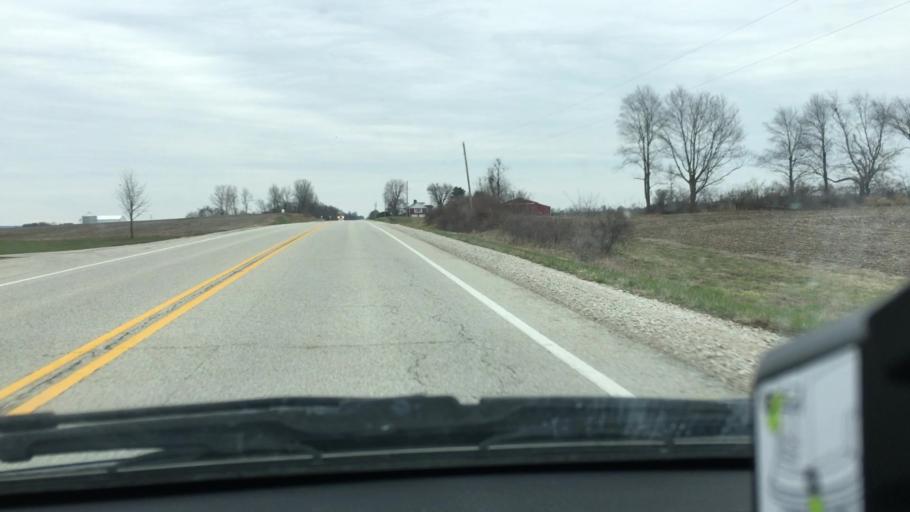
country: US
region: Indiana
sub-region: Daviess County
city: Odon
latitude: 38.9404
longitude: -87.0168
